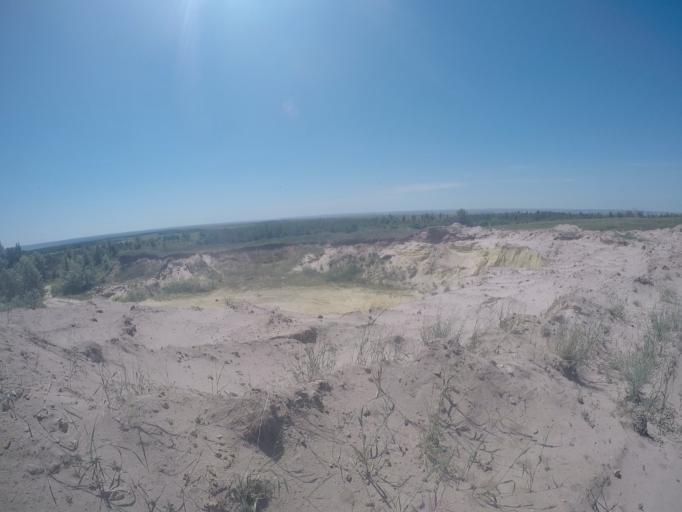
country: RU
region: Saratov
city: Krasnyy Oktyabr'
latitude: 51.2981
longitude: 45.5363
